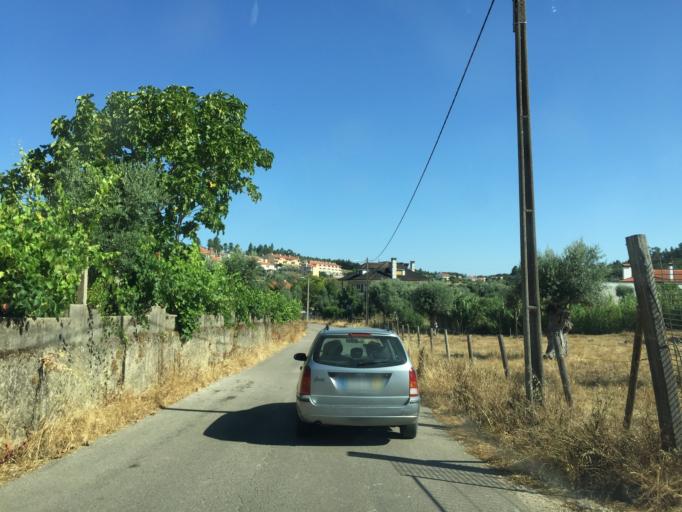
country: PT
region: Santarem
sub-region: Tomar
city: Tomar
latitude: 39.6068
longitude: -8.3310
